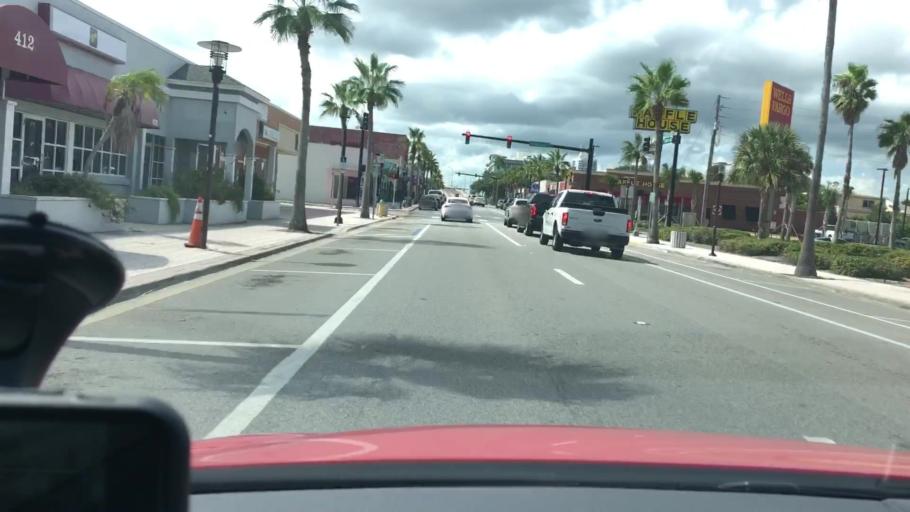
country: US
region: Florida
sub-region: Volusia County
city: Holly Hill
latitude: 29.2346
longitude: -81.0152
